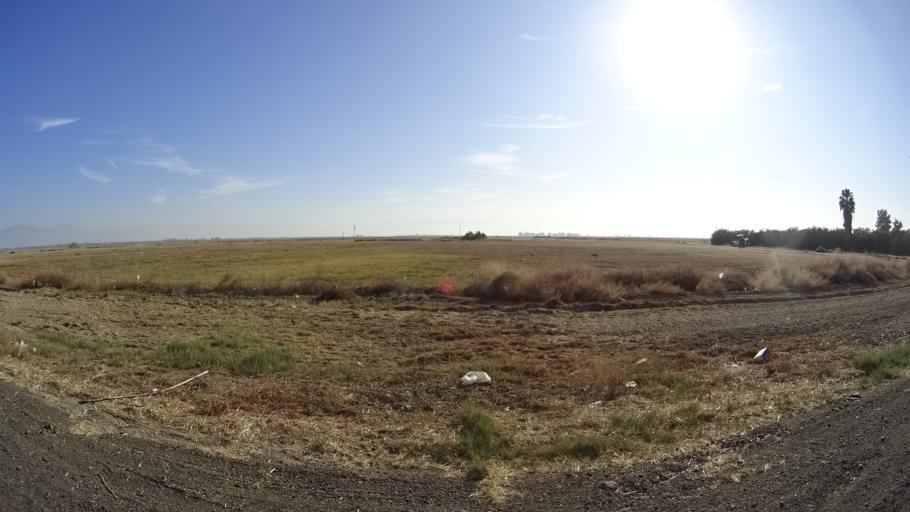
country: US
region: California
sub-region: Kern County
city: Greenfield
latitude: 35.2960
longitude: -118.9668
